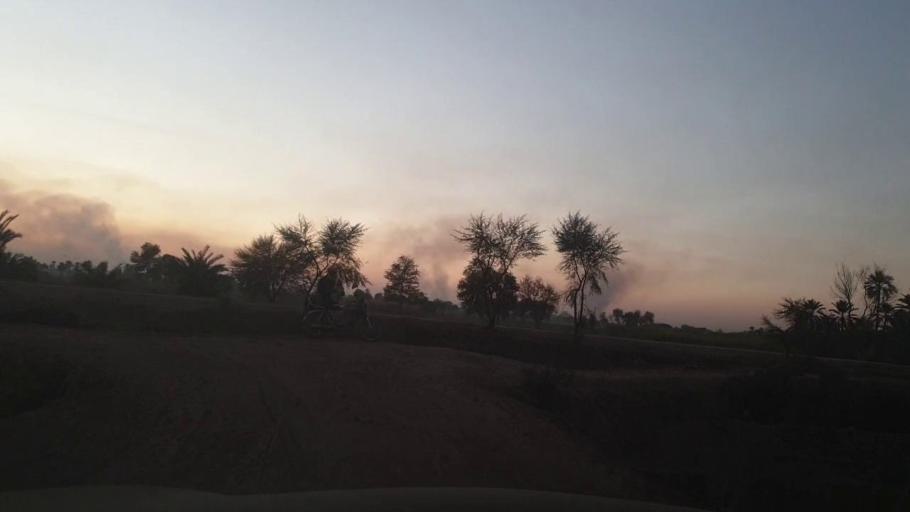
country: PK
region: Sindh
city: Ghotki
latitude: 28.0359
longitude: 69.3450
